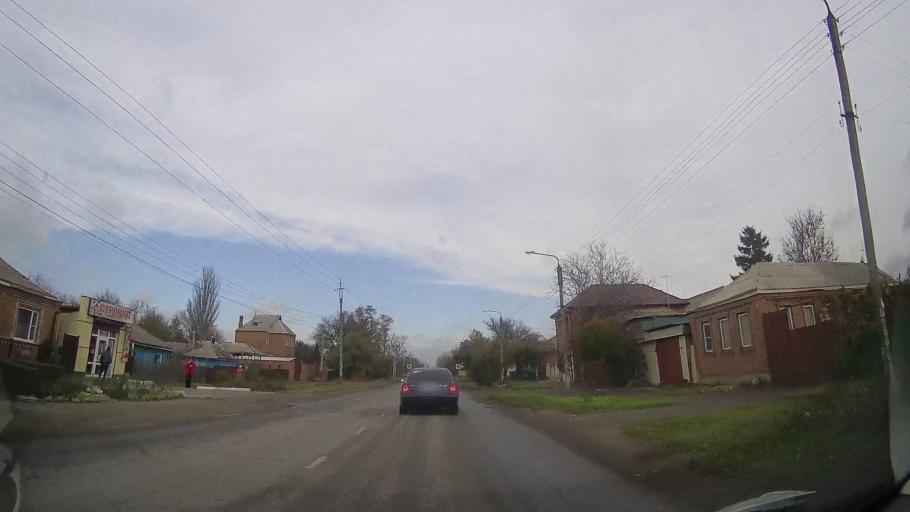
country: RU
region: Rostov
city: Bataysk
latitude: 47.1434
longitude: 39.7671
